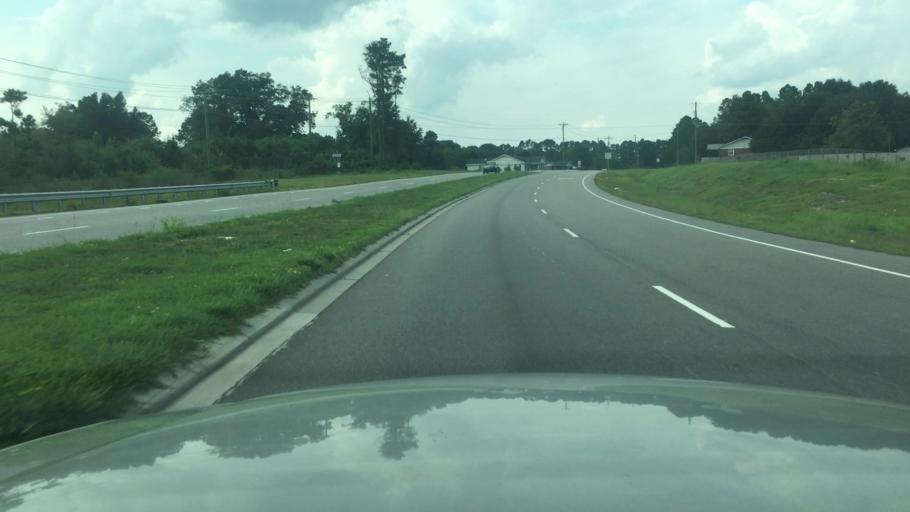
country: US
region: North Carolina
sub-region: Cumberland County
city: Spring Lake
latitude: 35.1432
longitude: -78.9095
